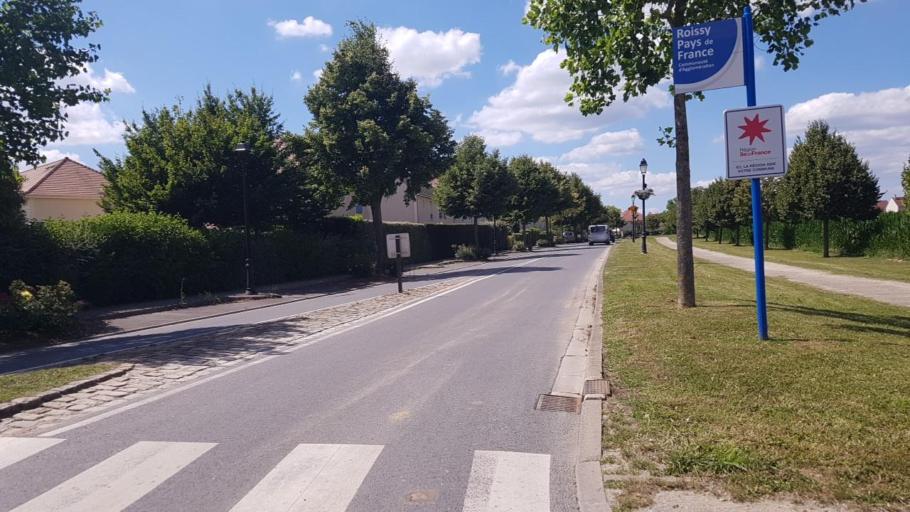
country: FR
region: Ile-de-France
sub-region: Departement de Seine-et-Marne
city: Moussy-le-Neuf
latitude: 49.0591
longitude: 2.6110
